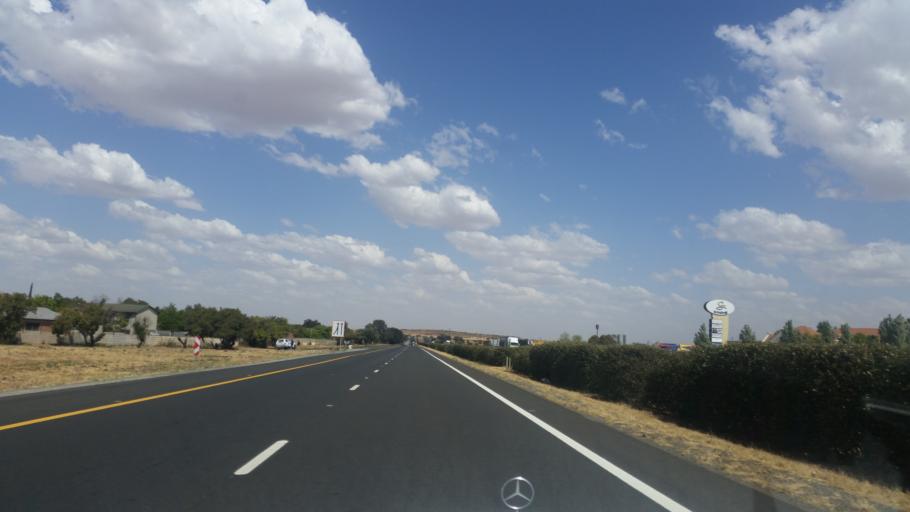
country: ZA
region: Orange Free State
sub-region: Mangaung Metropolitan Municipality
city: Bloemfontein
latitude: -29.1665
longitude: 26.1822
